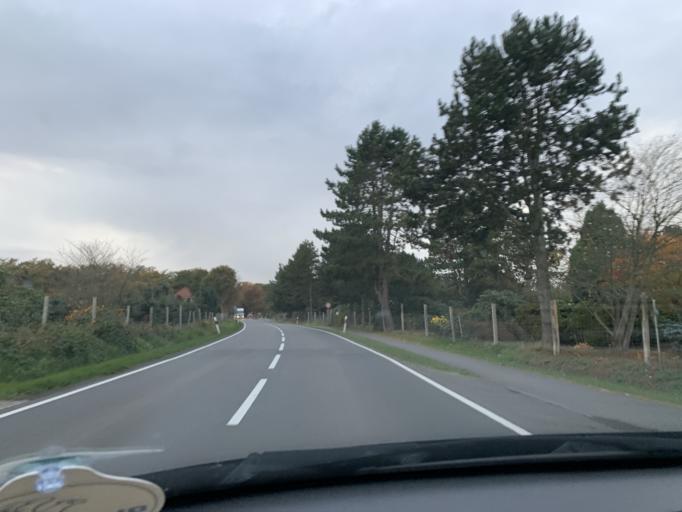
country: DE
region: Lower Saxony
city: Westerstede
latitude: 53.2854
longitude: 7.9881
